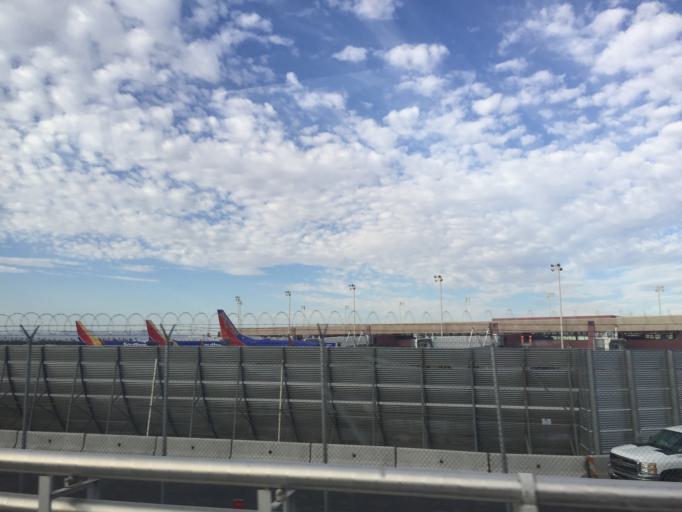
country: US
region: Nevada
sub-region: Clark County
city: Paradise
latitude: 36.0825
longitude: -115.1459
